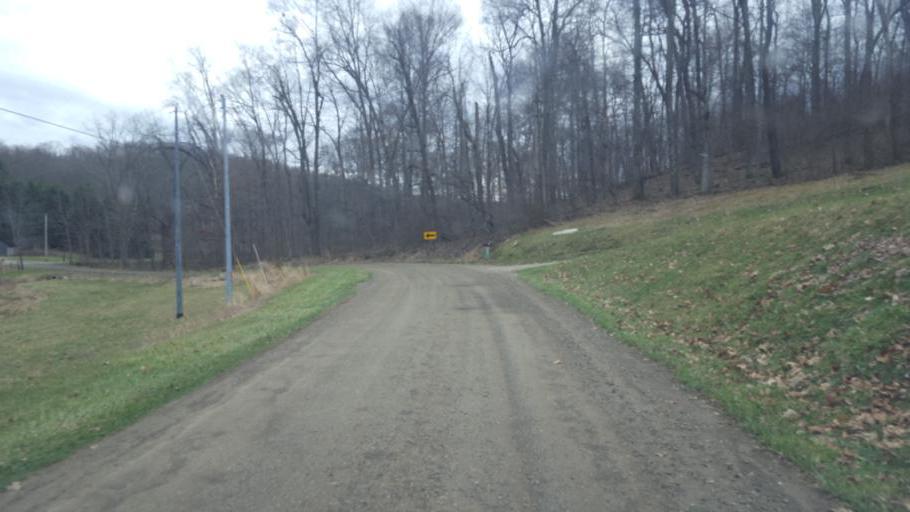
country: US
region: Ohio
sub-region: Licking County
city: Newark
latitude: 40.1712
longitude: -82.3149
